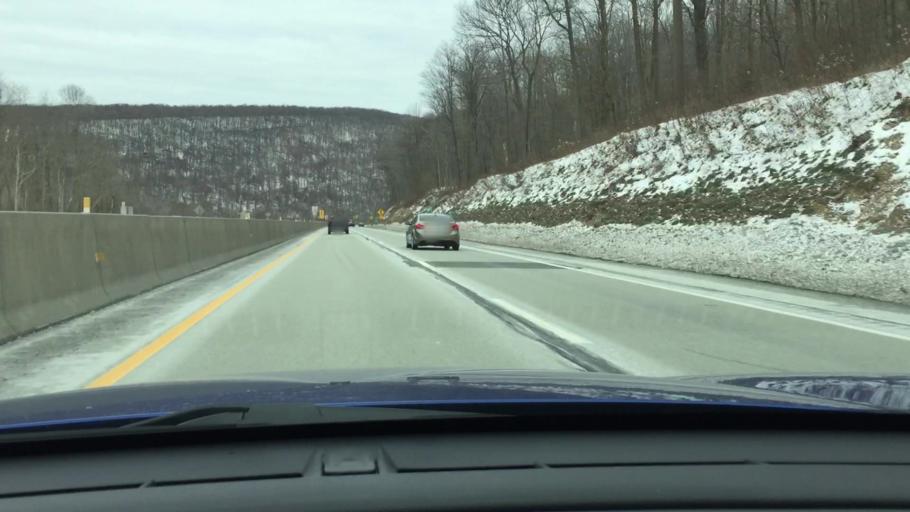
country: US
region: Pennsylvania
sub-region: Somerset County
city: Berlin
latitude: 39.9611
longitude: -78.8405
